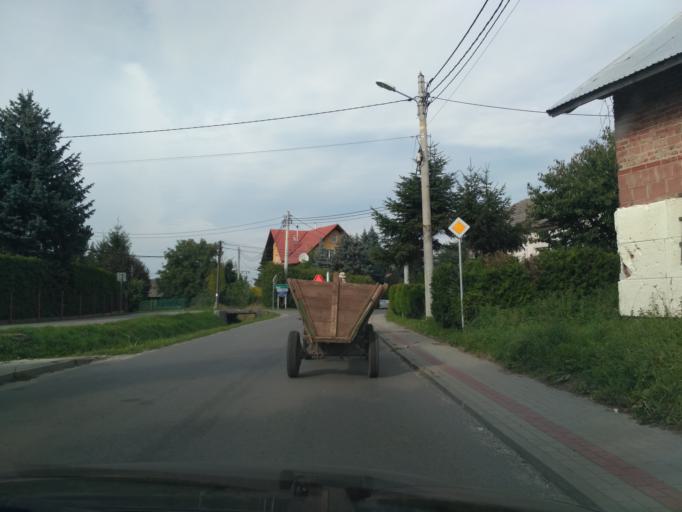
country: PL
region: Subcarpathian Voivodeship
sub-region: Powiat rzeszowski
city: Swilcza
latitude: 50.0791
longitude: 21.8998
